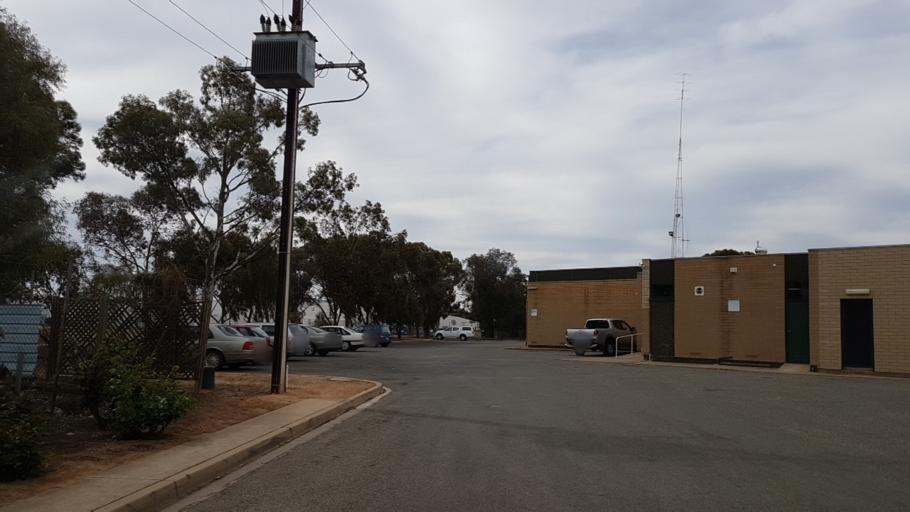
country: AU
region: South Australia
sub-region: Port Pirie City and Dists
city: Port Pirie
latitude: -33.1925
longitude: 138.0082
